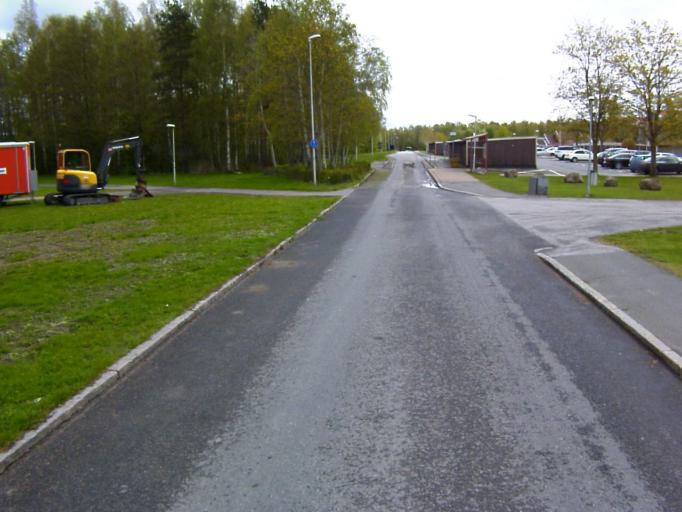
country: SE
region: Skane
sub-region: Kristianstads Kommun
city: Kristianstad
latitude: 56.0445
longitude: 14.1837
